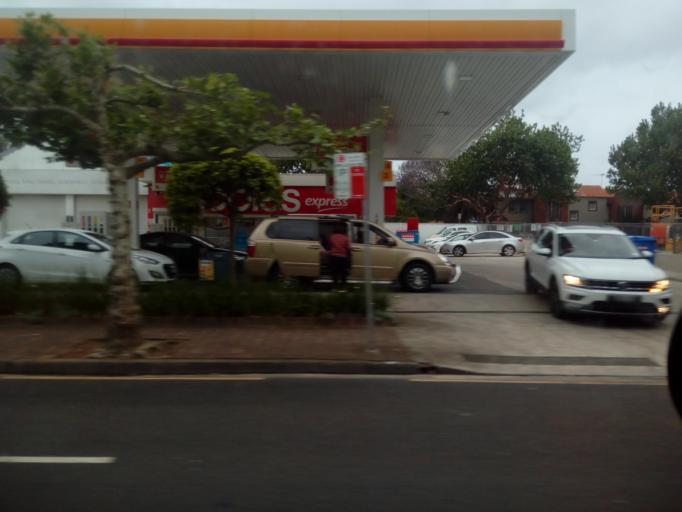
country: AU
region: New South Wales
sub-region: North Sydney
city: Cammeray
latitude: -33.8215
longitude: 151.2106
